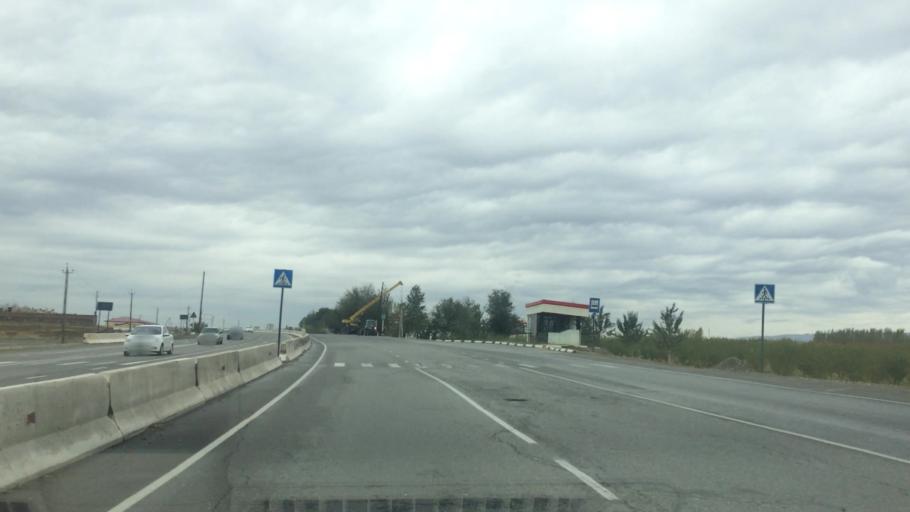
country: UZ
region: Jizzax
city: Jizzax
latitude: 39.9769
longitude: 67.5624
